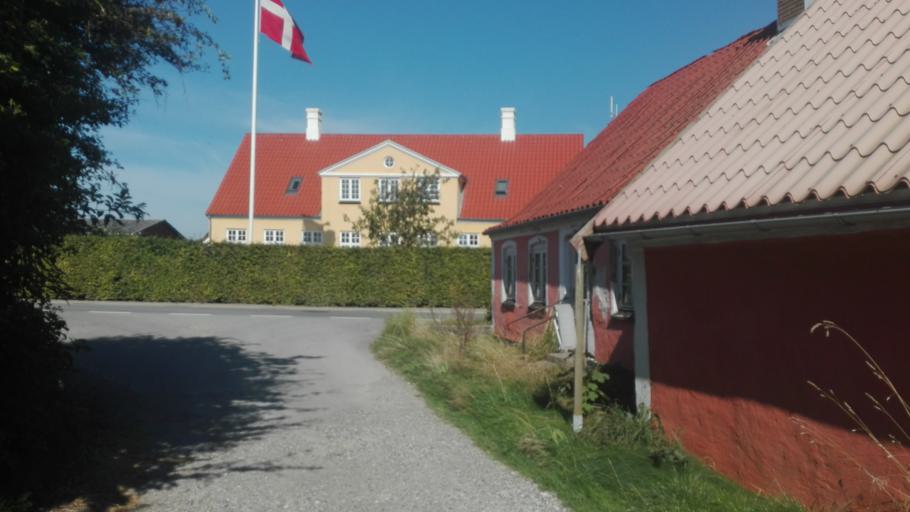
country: DK
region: Central Jutland
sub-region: Syddjurs Kommune
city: Ebeltoft
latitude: 56.2392
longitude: 10.7488
